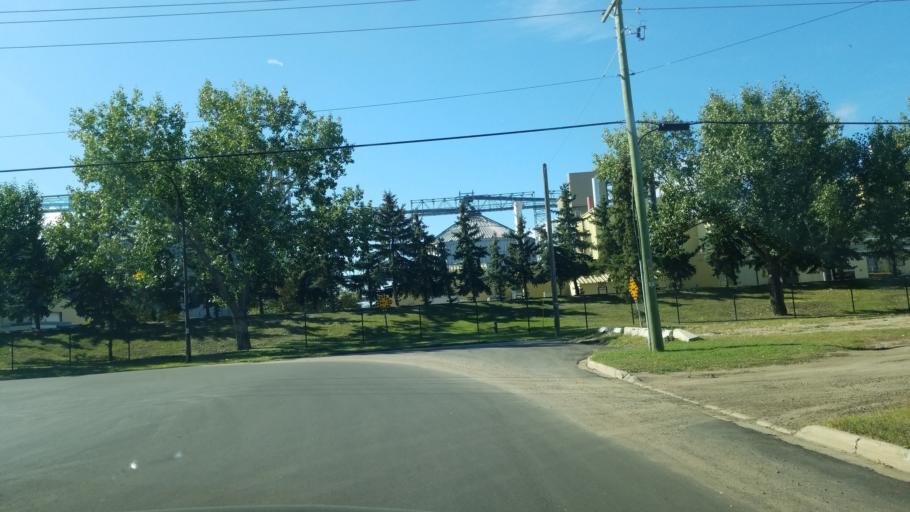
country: CA
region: Saskatchewan
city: Lloydminster
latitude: 53.2835
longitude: -110.0295
